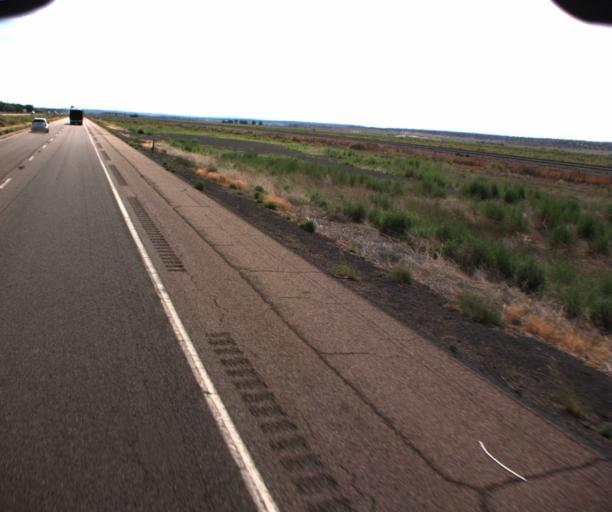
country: US
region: Arizona
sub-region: Apache County
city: Houck
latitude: 35.1981
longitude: -109.3989
